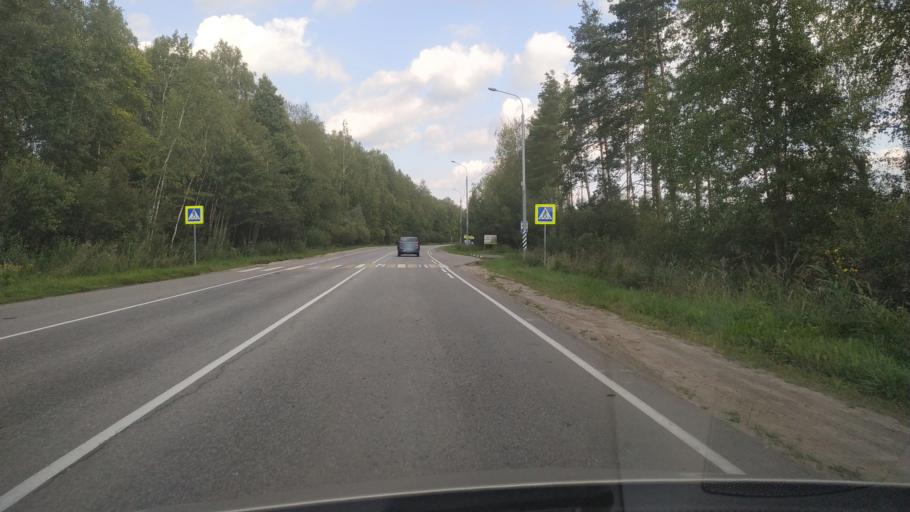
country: RU
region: Moskovskaya
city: Likino-Dulevo
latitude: 55.7294
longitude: 39.0136
